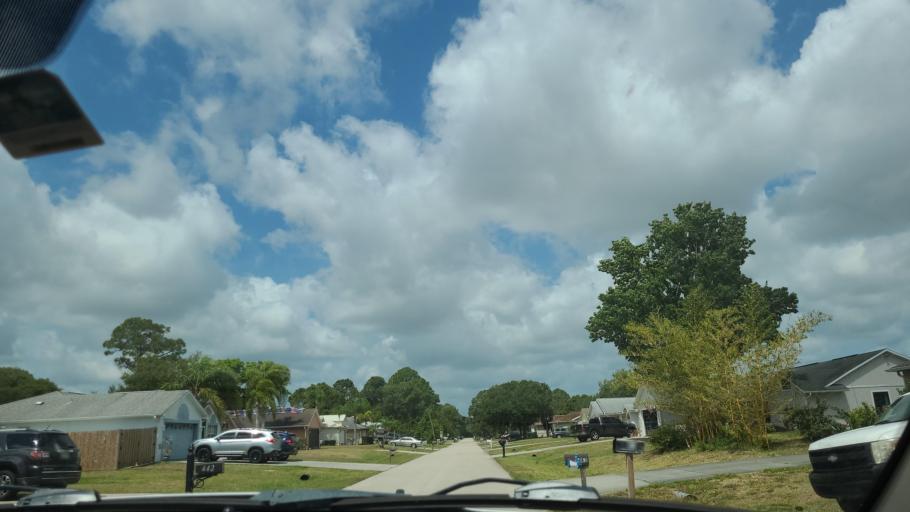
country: US
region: Florida
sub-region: Brevard County
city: West Melbourne
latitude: 28.0057
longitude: -80.6609
